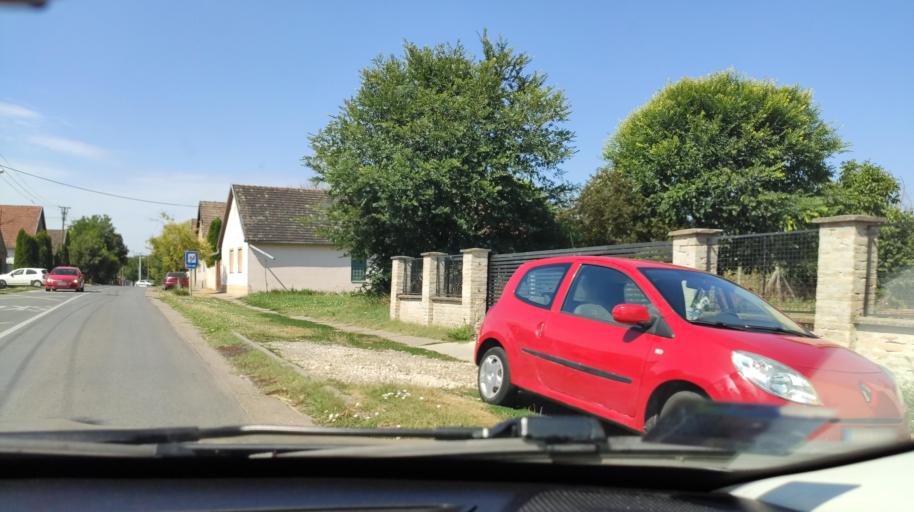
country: RS
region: Autonomna Pokrajina Vojvodina
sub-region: Severnobacki Okrug
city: Backa Topola
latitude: 45.8103
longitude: 19.6340
